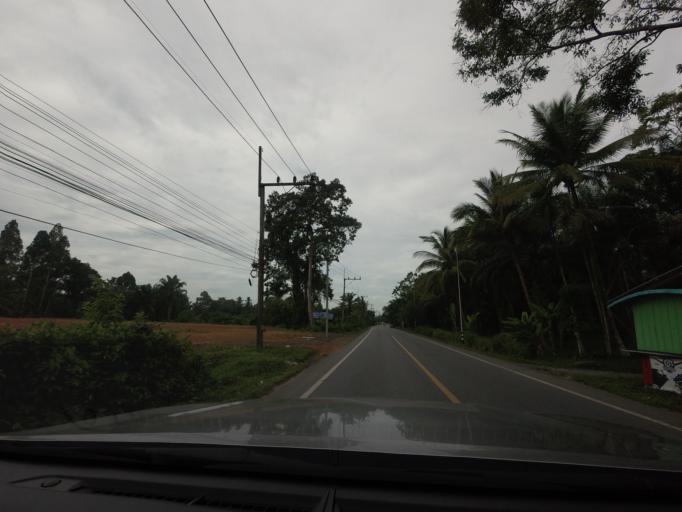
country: TH
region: Nakhon Si Thammarat
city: Phra Phrom
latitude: 8.3166
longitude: 99.9455
